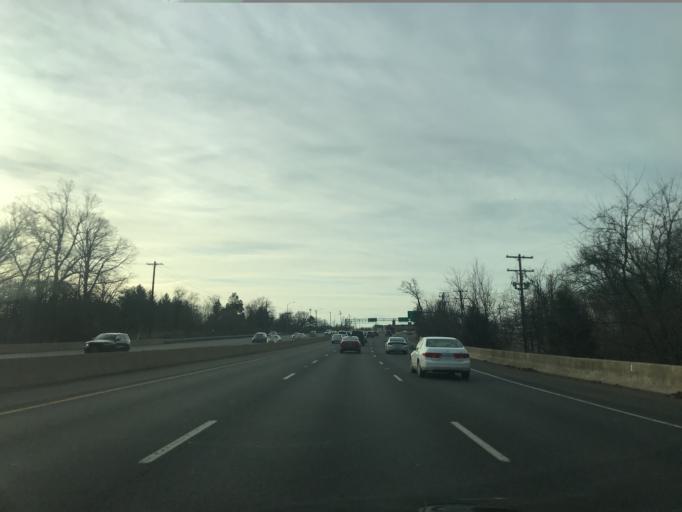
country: US
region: Maryland
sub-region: Prince George's County
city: Camp Springs
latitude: 38.7907
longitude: -76.8980
